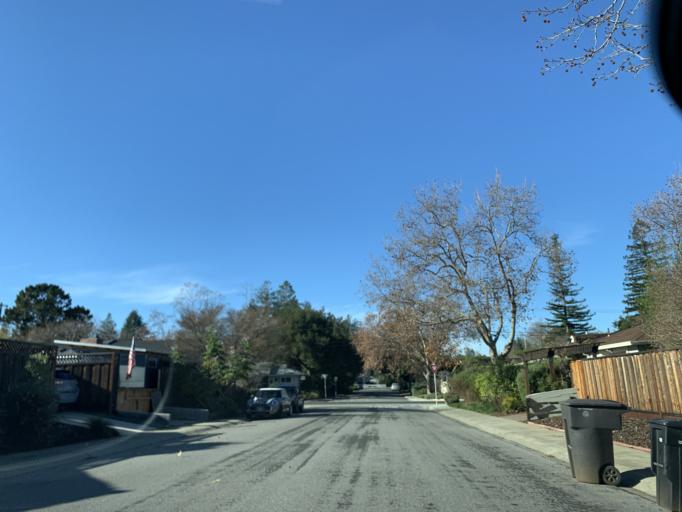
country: US
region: California
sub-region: Santa Clara County
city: Los Altos
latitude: 37.3912
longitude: -122.1028
